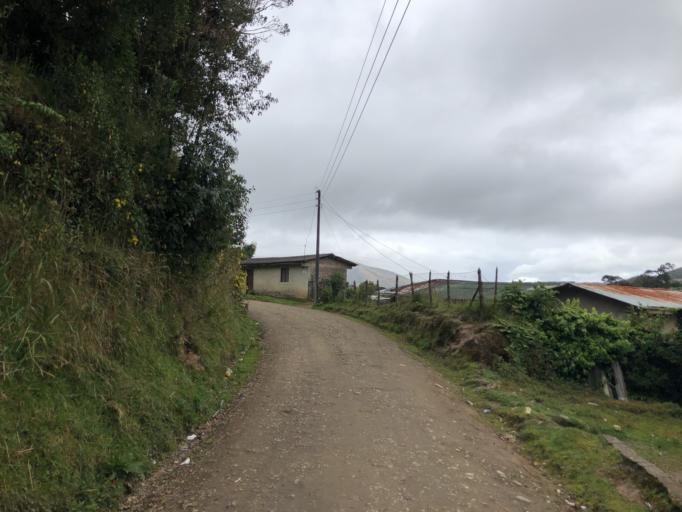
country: CO
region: Cauca
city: Totoro
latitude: 2.4949
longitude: -76.3464
